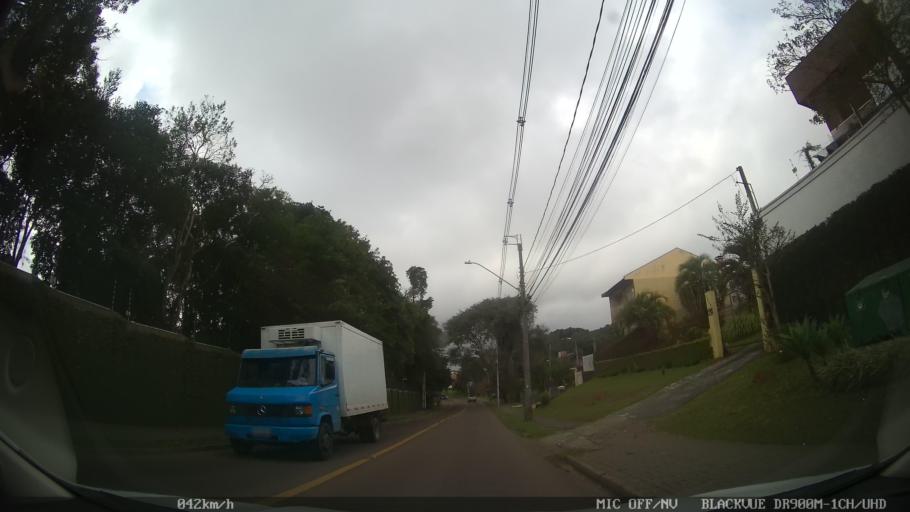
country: BR
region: Parana
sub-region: Curitiba
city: Curitiba
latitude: -25.3709
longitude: -49.2328
